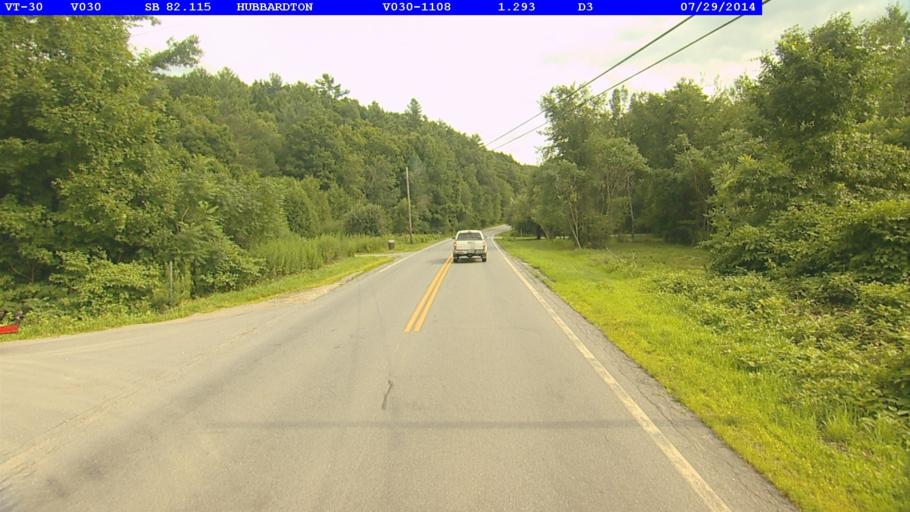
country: US
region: Vermont
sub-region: Rutland County
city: Castleton
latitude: 43.6967
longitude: -73.1843
